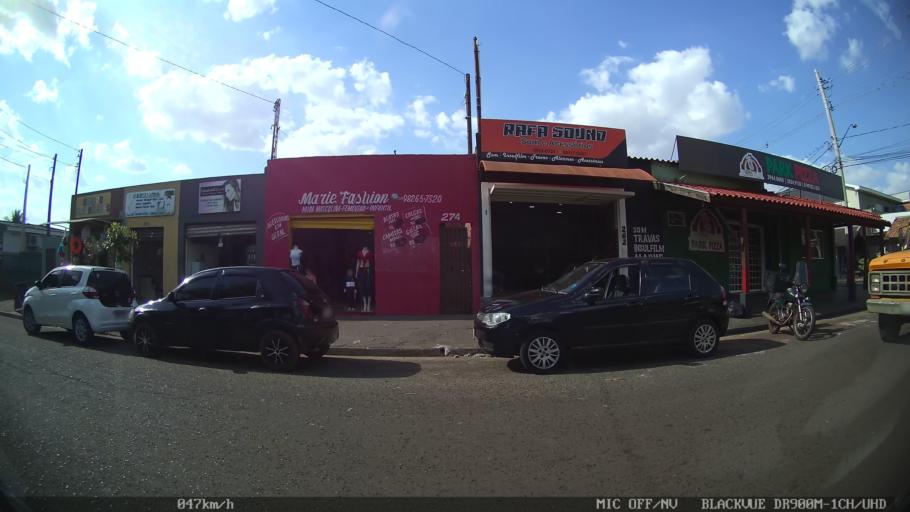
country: BR
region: Sao Paulo
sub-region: Ribeirao Preto
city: Ribeirao Preto
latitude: -21.2013
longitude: -47.8443
